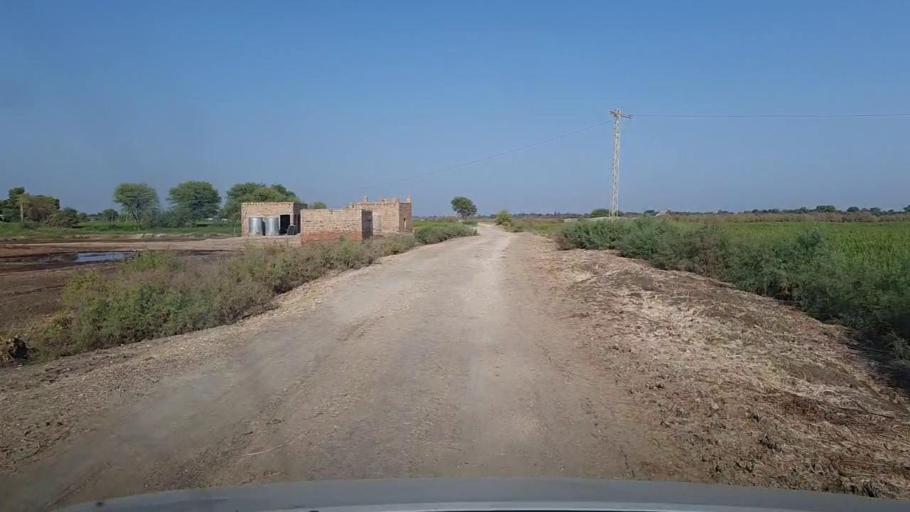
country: PK
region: Sindh
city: Kandhkot
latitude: 28.2792
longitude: 69.3194
